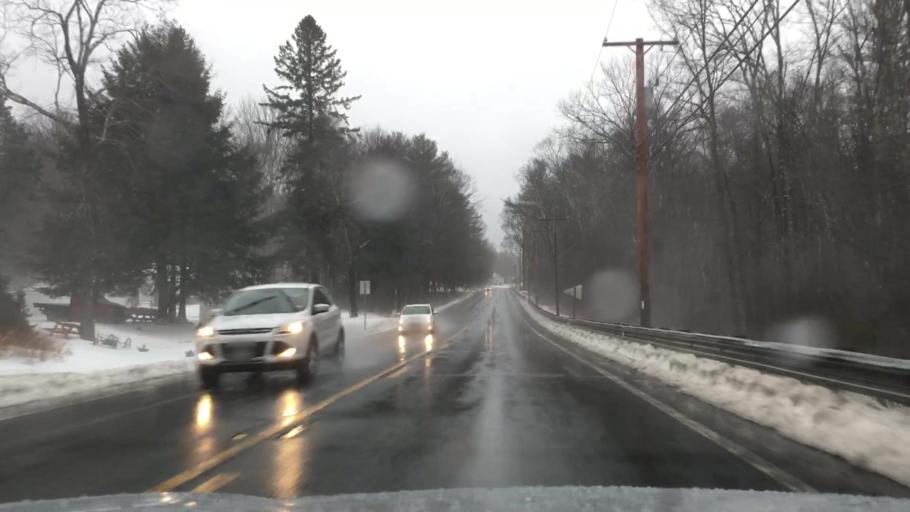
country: US
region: Massachusetts
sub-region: Hampshire County
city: Belchertown
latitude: 42.3058
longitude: -72.4061
